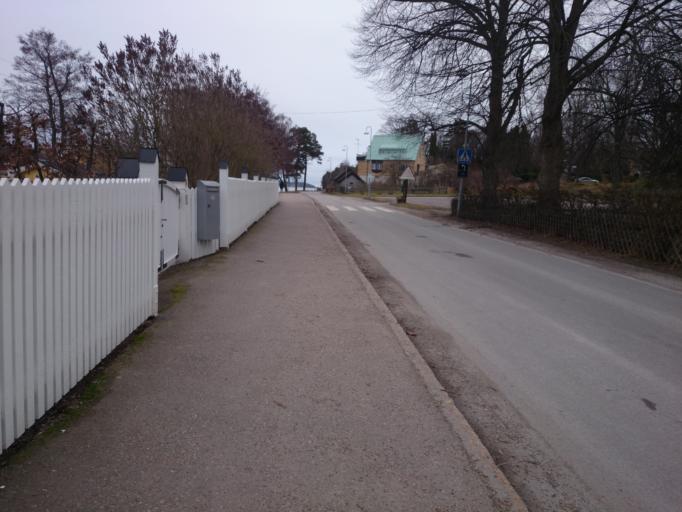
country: SE
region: Stockholm
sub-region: Nynashamns Kommun
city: Nynashamn
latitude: 58.8939
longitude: 17.9420
